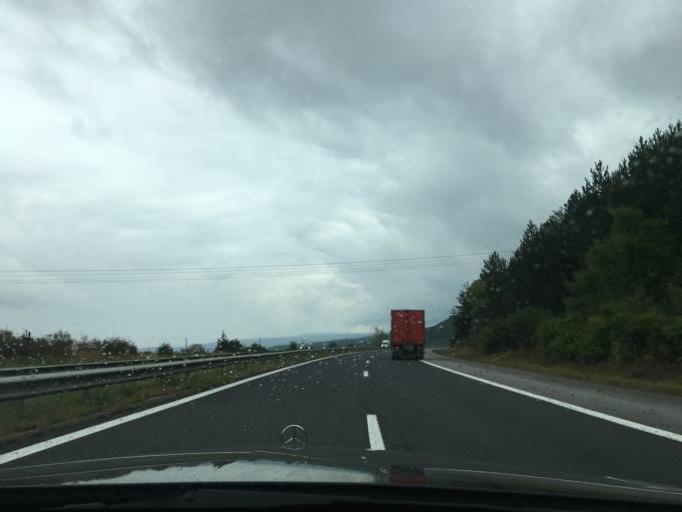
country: BG
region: Sofiya
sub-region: Obshtina Elin Pelin
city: Elin Pelin
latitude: 42.5972
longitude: 23.5853
